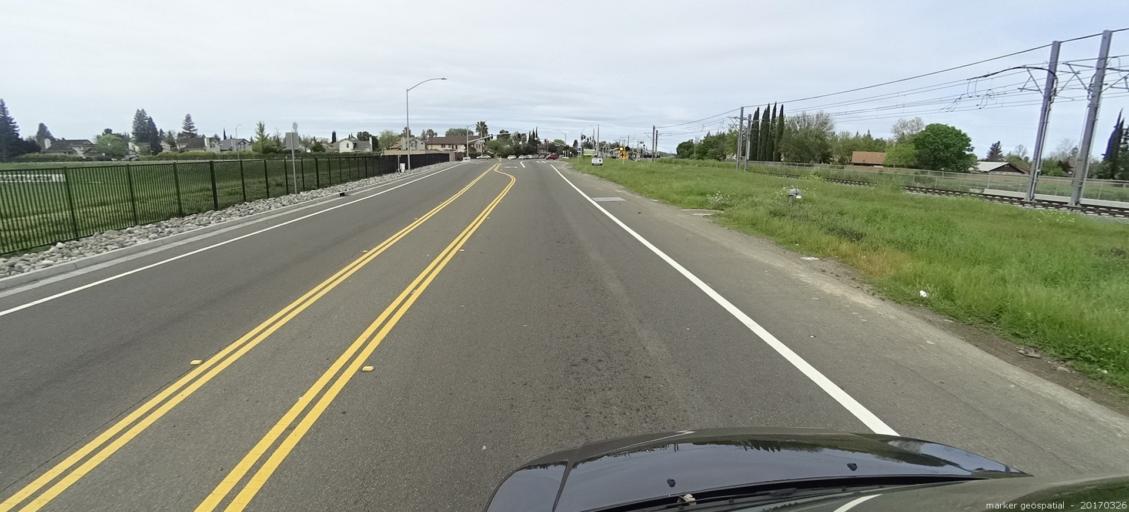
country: US
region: California
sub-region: Sacramento County
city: Laguna
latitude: 38.4581
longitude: -121.4263
